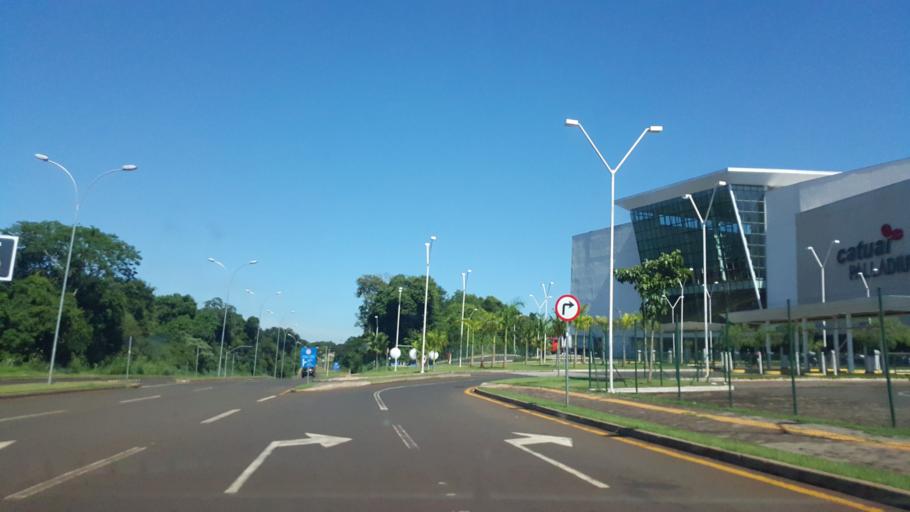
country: AR
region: Misiones
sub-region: Departamento de Iguazu
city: Puerto Iguazu
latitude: -25.5698
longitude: -54.5571
